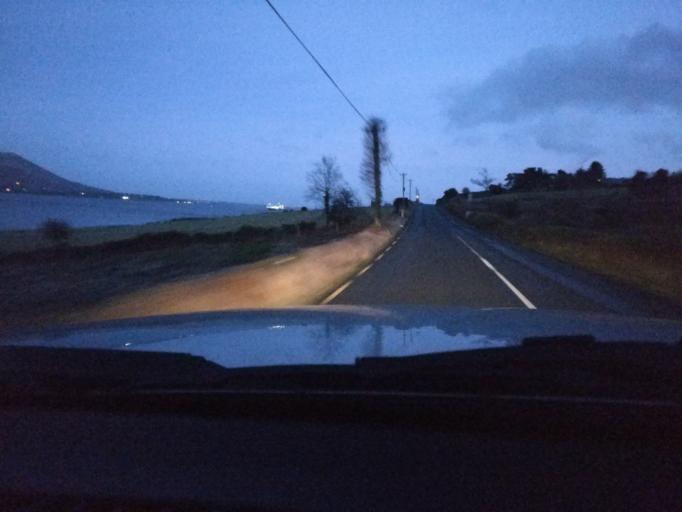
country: GB
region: Northern Ireland
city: Rostrevor
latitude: 54.0657
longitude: -6.2173
